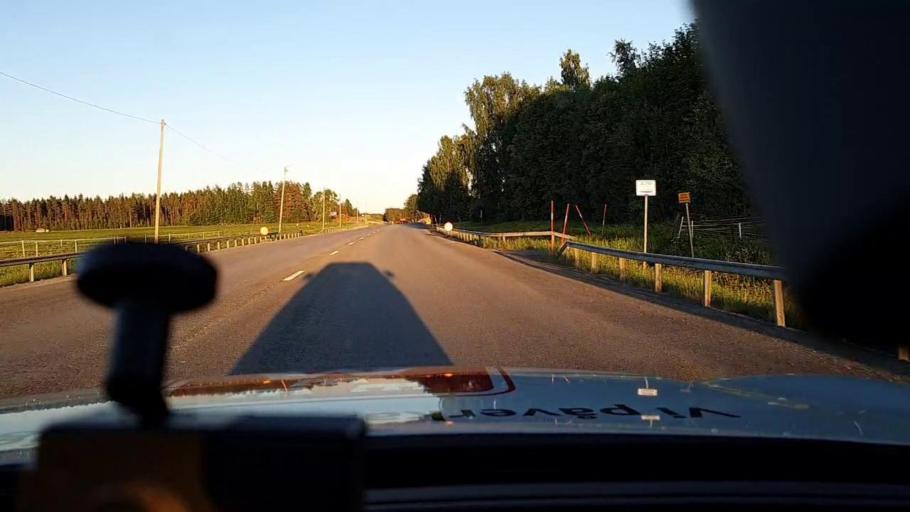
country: SE
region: Norrbotten
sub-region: Bodens Kommun
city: Saevast
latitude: 65.7243
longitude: 21.7874
